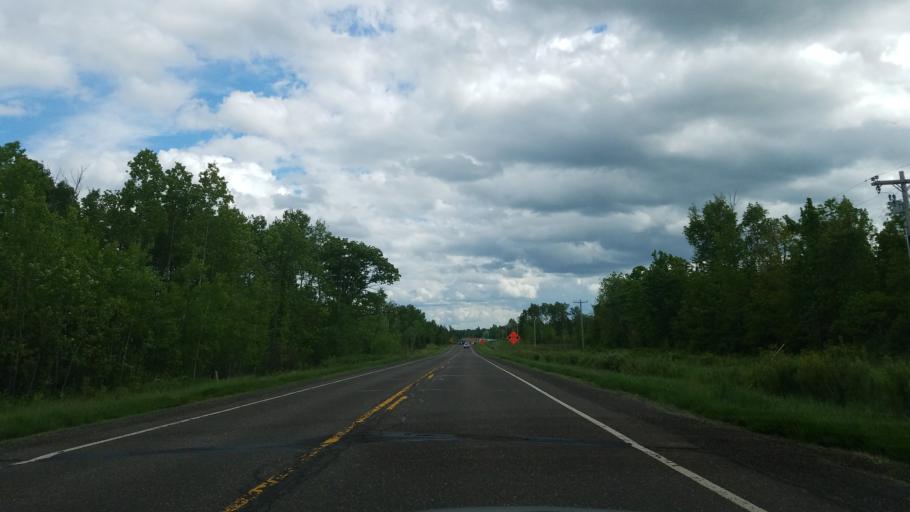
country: US
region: Wisconsin
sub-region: Douglas County
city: Superior
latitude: 46.2409
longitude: -92.1544
